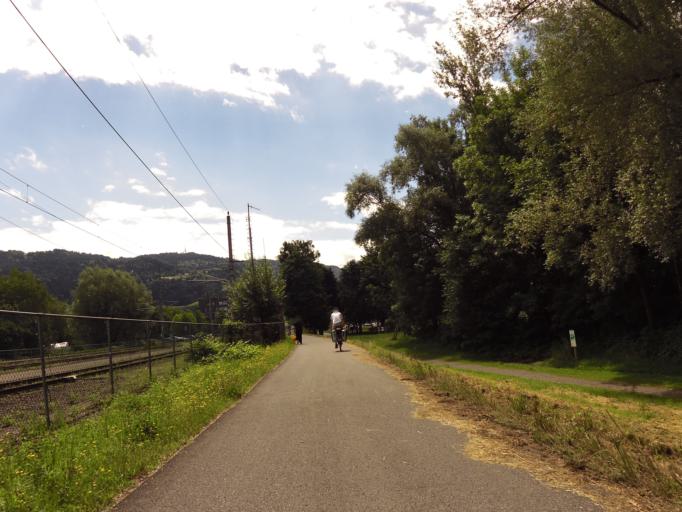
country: AT
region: Vorarlberg
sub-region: Politischer Bezirk Bregenz
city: Lochau
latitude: 47.5311
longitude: 9.7403
